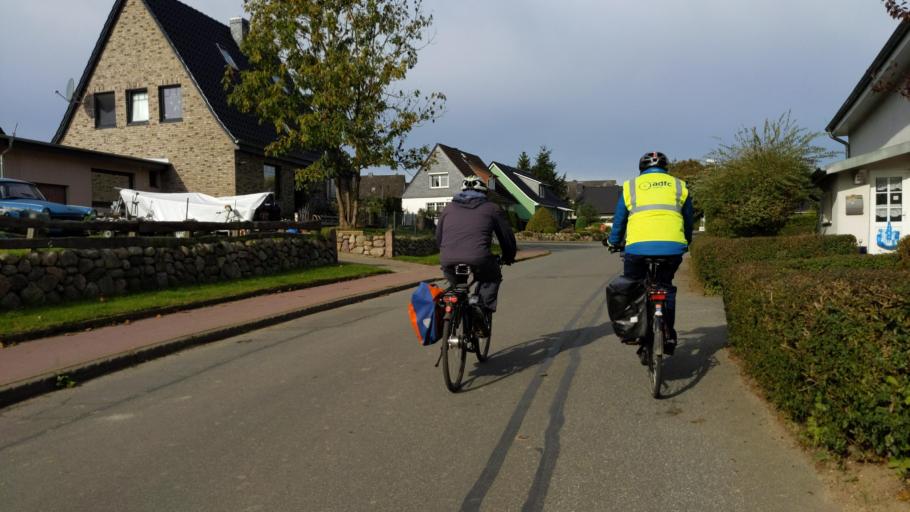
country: DE
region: Schleswig-Holstein
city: Zarpen
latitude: 53.8730
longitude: 10.5161
